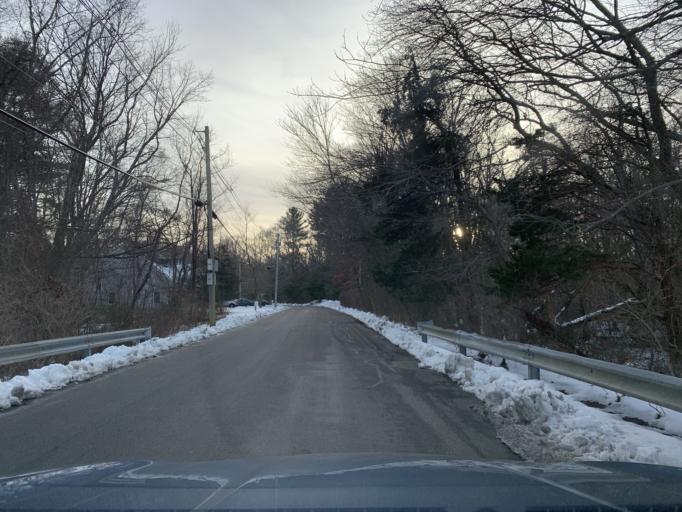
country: US
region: Rhode Island
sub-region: Washington County
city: North Kingstown
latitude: 41.5944
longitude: -71.4412
